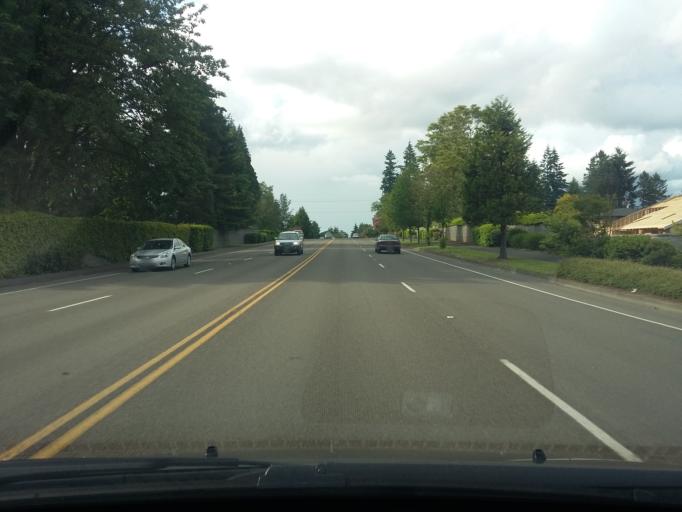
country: US
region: Washington
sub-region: Clark County
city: Walnut Grove
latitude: 45.6718
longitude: -122.6032
